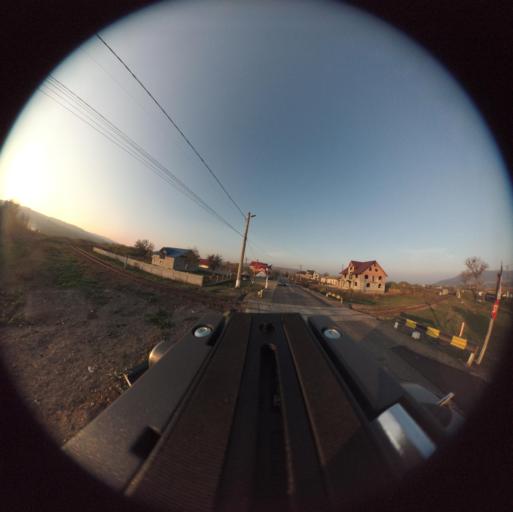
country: RO
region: Vaslui
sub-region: Comuna Bacesti
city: Bacesti
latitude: 46.8273
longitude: 27.2507
